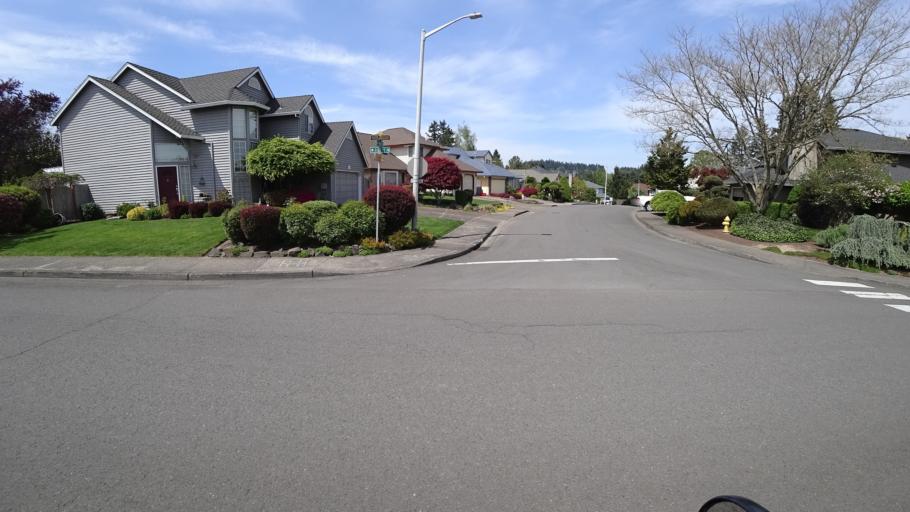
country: US
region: Oregon
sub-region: Washington County
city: Aloha
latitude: 45.4608
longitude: -122.8390
